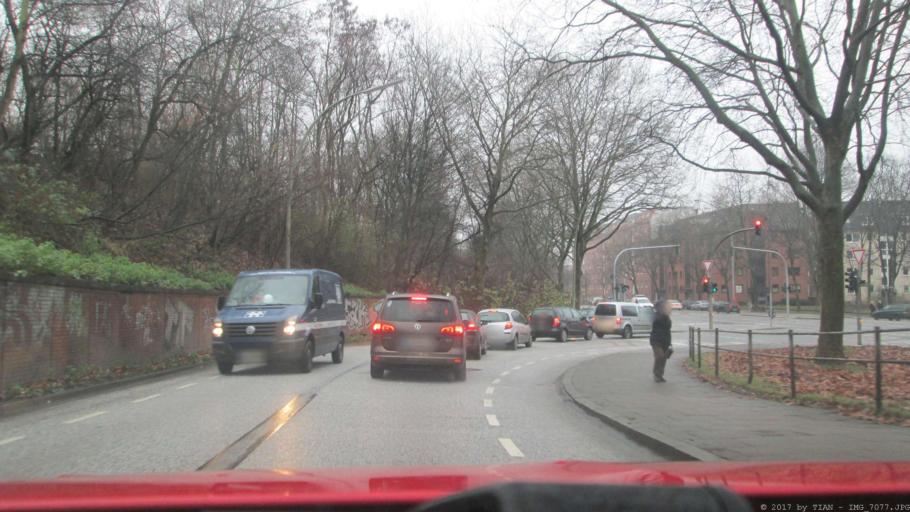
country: DE
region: Hamburg
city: Borgfelde
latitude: 53.5554
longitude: 10.0561
